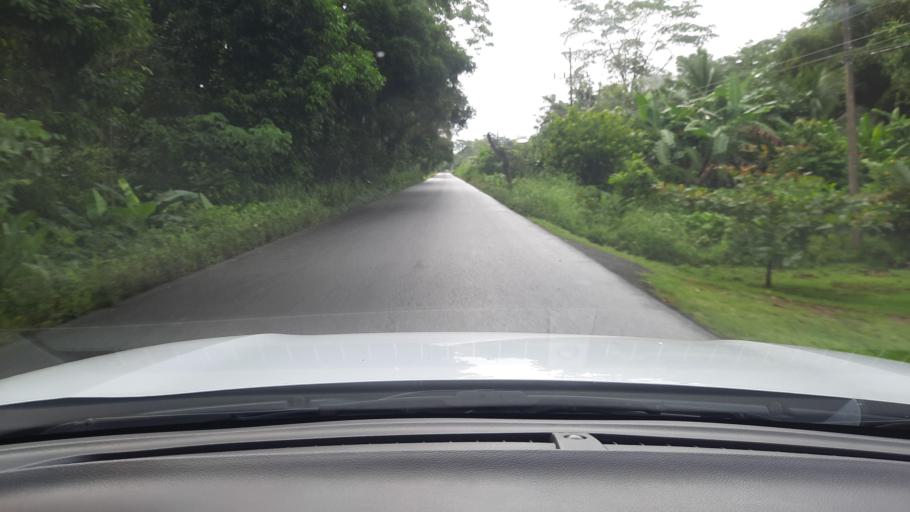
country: CR
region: Alajuela
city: Upala
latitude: 10.9257
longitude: -85.0746
